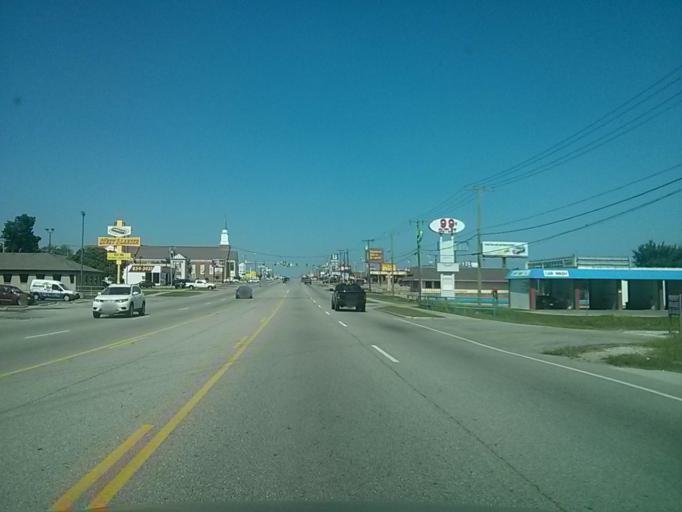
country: US
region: Oklahoma
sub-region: Tulsa County
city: Tulsa
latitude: 36.1608
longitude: -95.8933
